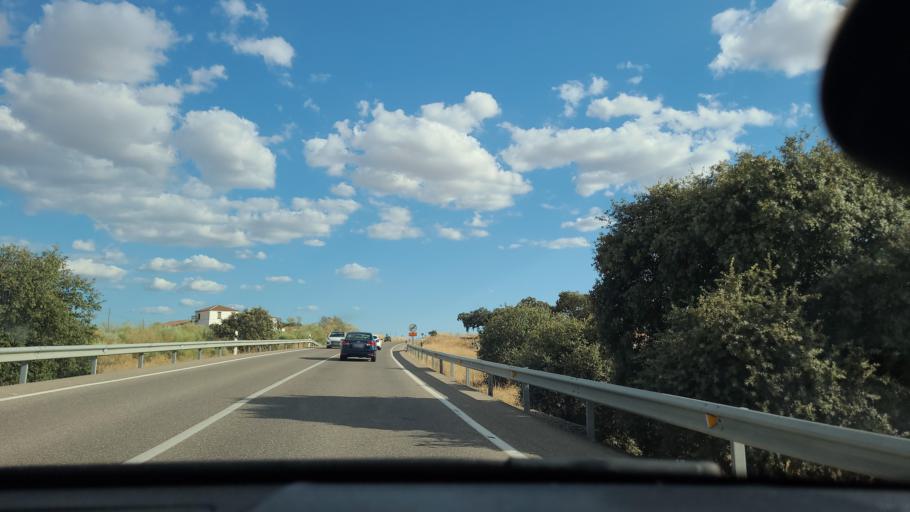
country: ES
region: Extremadura
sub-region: Provincia de Badajoz
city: Granja de Torrehermosa
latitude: 38.2836
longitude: -5.5195
